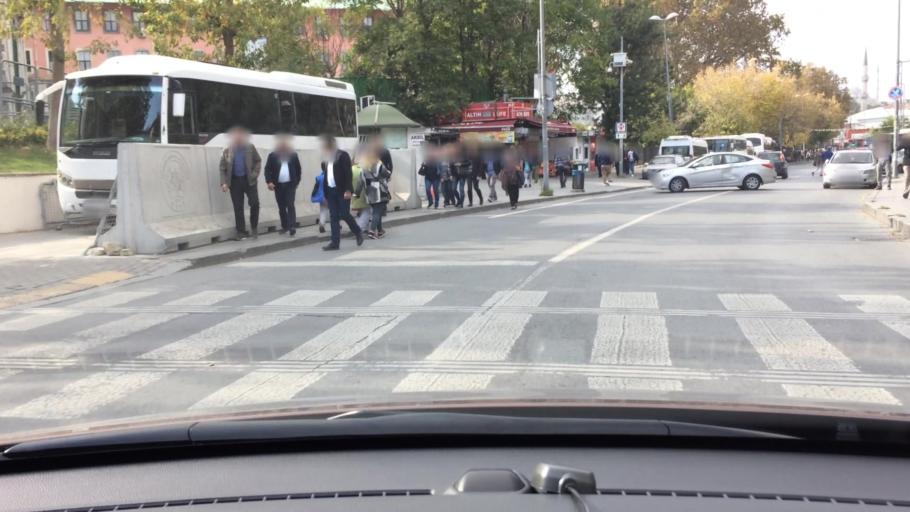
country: TR
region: Istanbul
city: Istanbul
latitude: 41.0107
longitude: 28.9614
